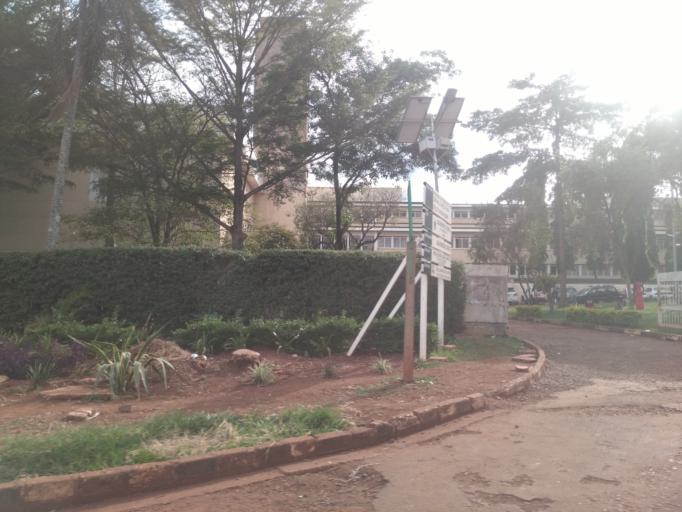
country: UG
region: Eastern Region
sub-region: Jinja District
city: Jinja
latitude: 0.4227
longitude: 33.2077
